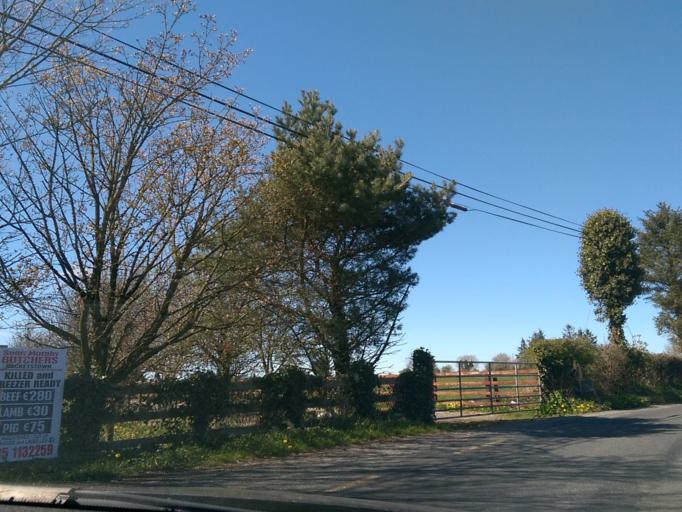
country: IE
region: Leinster
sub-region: Wicklow
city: Baltinglass
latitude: 52.8830
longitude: -6.5897
